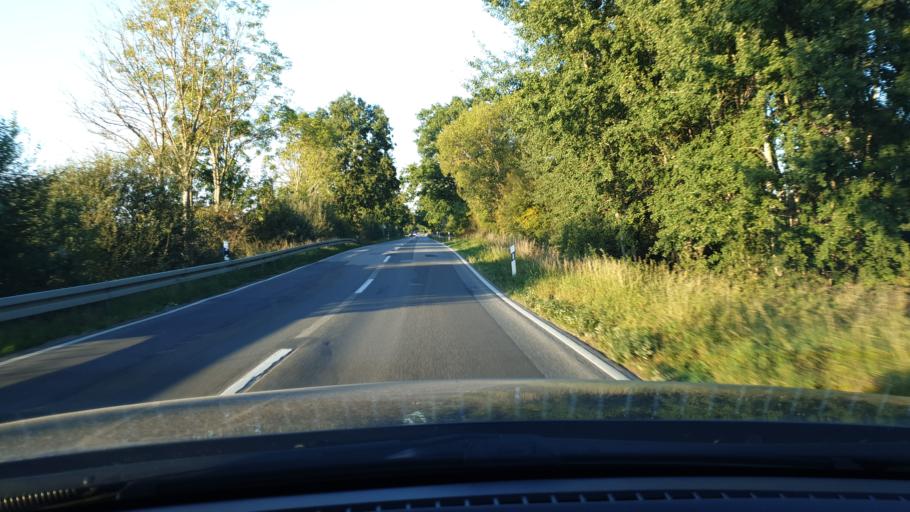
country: DE
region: Mecklenburg-Vorpommern
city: Lutzow
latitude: 53.6061
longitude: 11.1379
